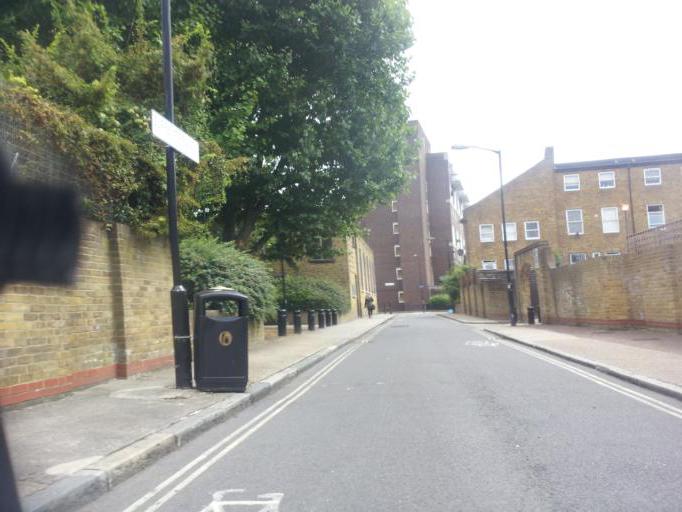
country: GB
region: England
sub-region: Greater London
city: Camberwell
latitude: 51.4899
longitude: -0.0817
